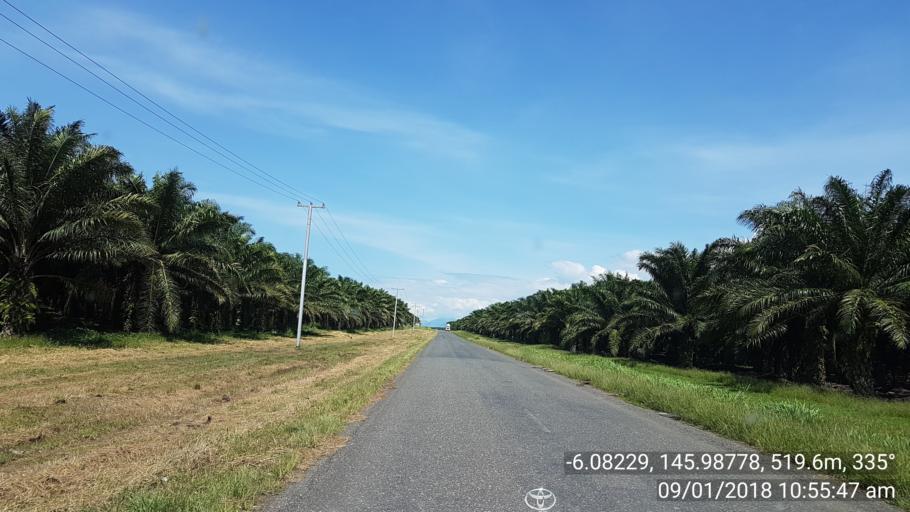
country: PG
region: Eastern Highlands
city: Kainantu
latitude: -6.0825
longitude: 145.9881
